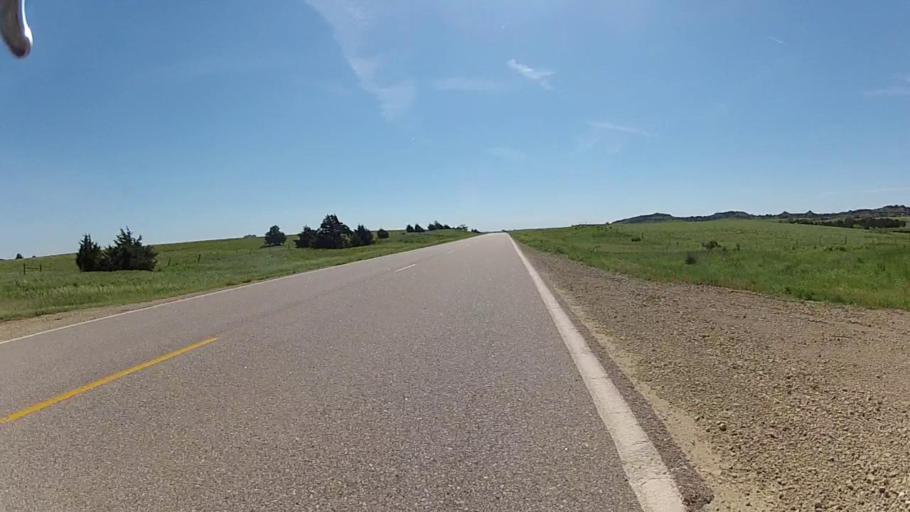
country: US
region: Kansas
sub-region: Barber County
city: Medicine Lodge
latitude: 37.2753
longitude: -98.7253
